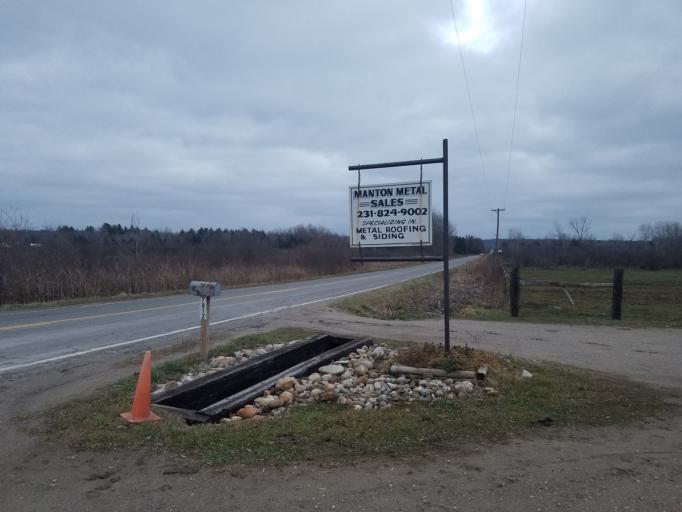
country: US
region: Michigan
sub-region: Wexford County
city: Manton
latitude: 44.4250
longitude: -85.4221
